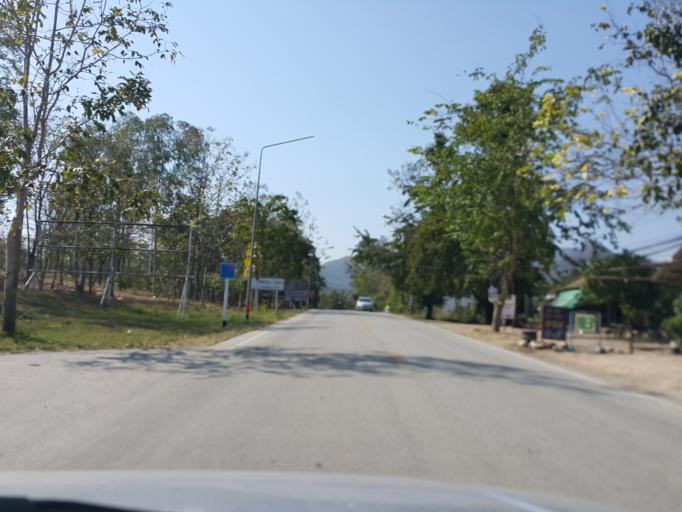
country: TH
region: Chiang Mai
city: Mae Wang
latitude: 18.6158
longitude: 98.7765
